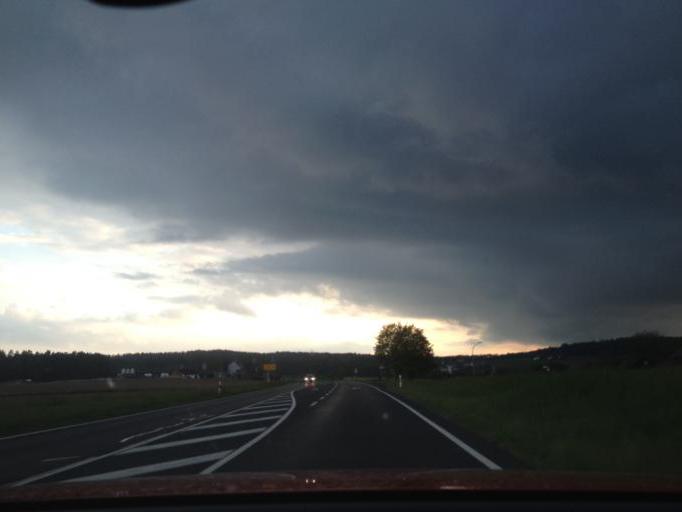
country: DE
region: Bavaria
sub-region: Upper Palatinate
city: Sulzbach-Rosenberg
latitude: 49.5282
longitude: 11.7624
